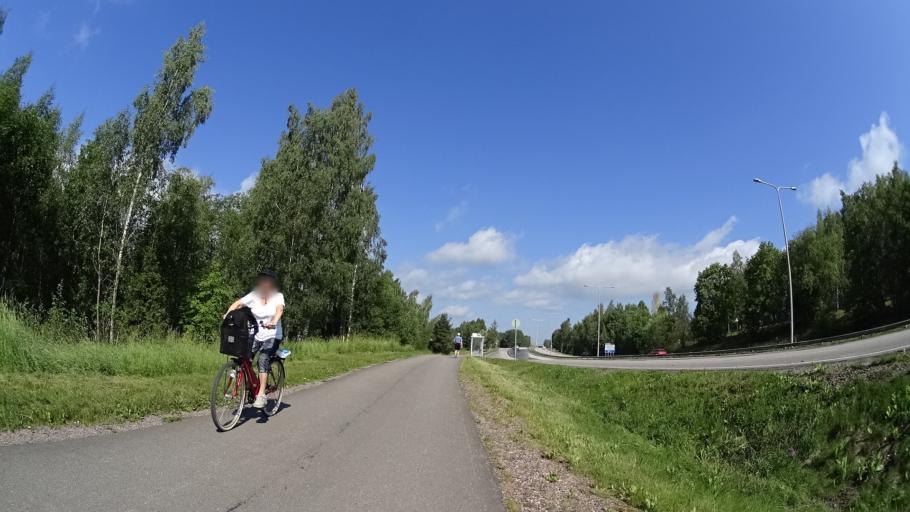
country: FI
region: Uusimaa
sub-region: Helsinki
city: Teekkarikylae
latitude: 60.2739
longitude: 24.8716
